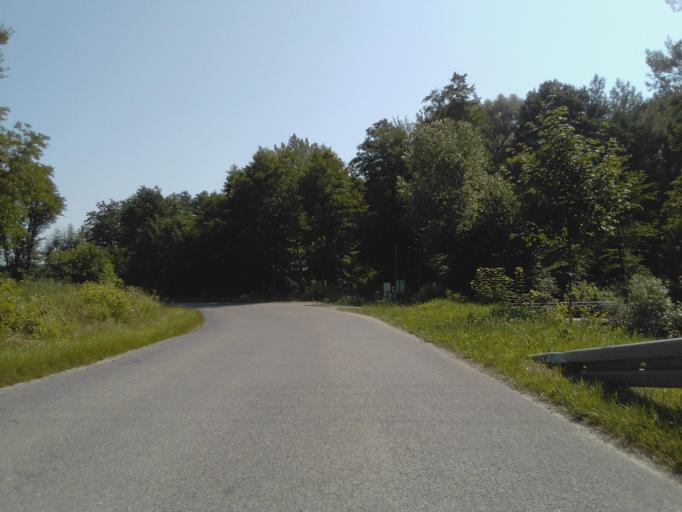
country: PL
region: Subcarpathian Voivodeship
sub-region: Powiat ropczycko-sedziszowski
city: Zagorzyce
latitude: 50.0320
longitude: 21.6492
